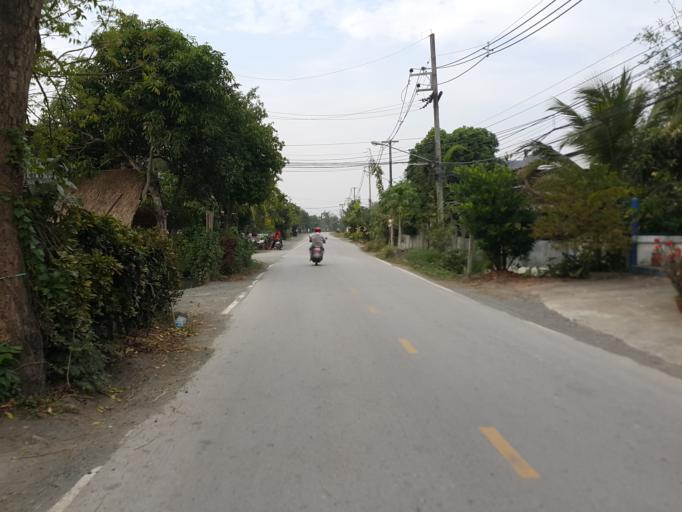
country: TH
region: Chiang Mai
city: San Kamphaeng
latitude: 18.8359
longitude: 99.1521
